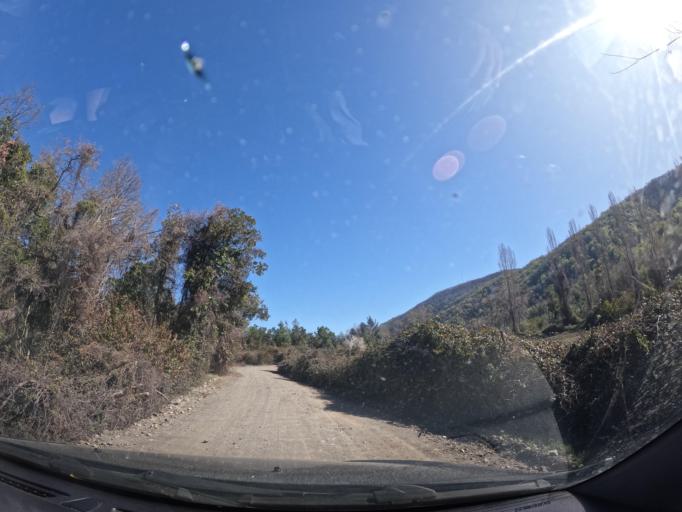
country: CL
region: Maule
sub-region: Provincia de Linares
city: Longavi
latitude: -36.2273
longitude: -71.3824
